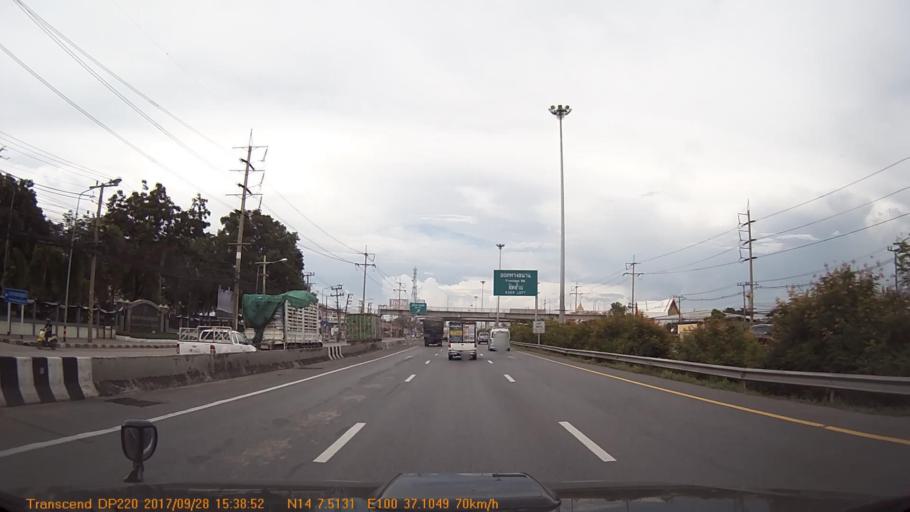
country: TH
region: Pathum Thani
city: Khlong Luang
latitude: 14.1260
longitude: 100.6184
